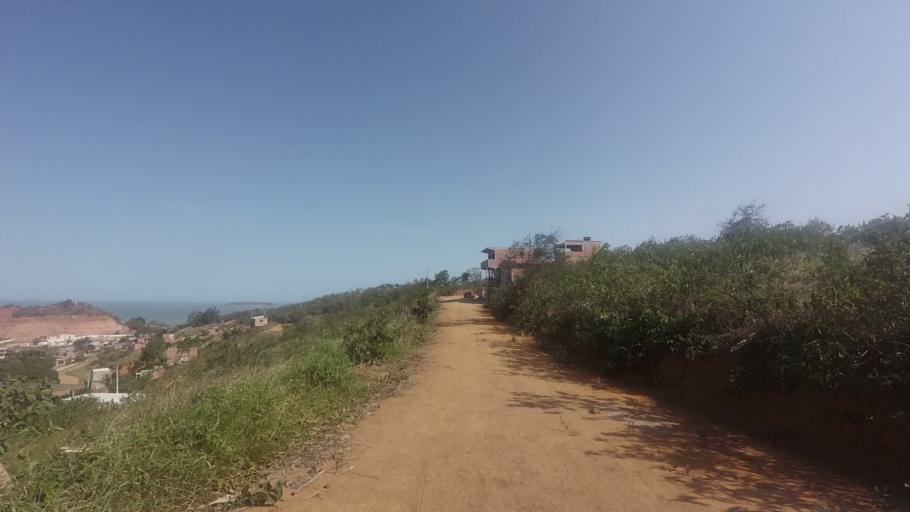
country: BR
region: Espirito Santo
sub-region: Piuma
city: Piuma
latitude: -20.8850
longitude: -40.7729
